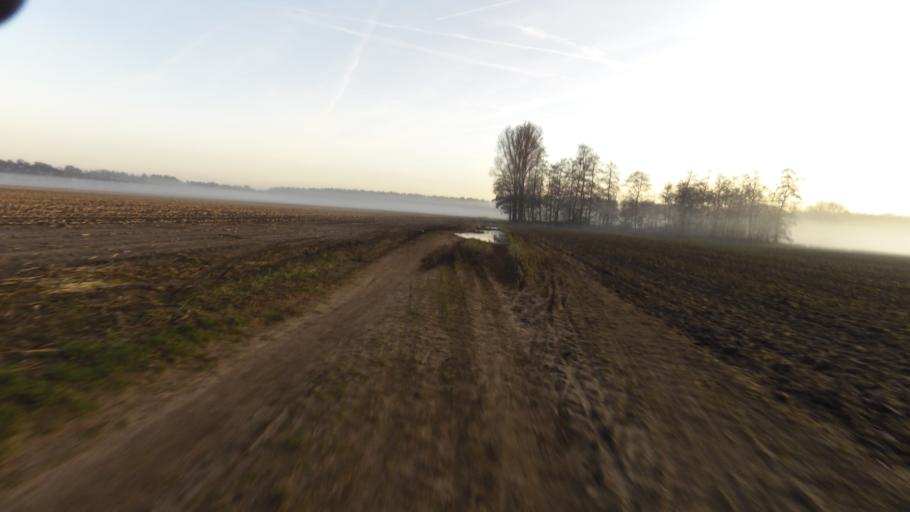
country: NL
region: Gelderland
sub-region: Gemeente Apeldoorn
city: Uddel
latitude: 52.2432
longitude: 5.7856
